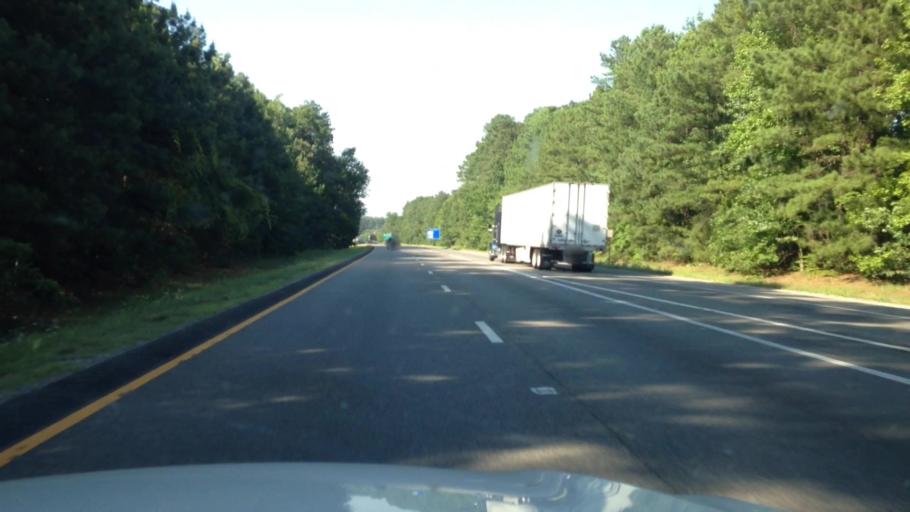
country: US
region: Virginia
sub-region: City of Petersburg
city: Petersburg
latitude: 37.0664
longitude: -77.3703
